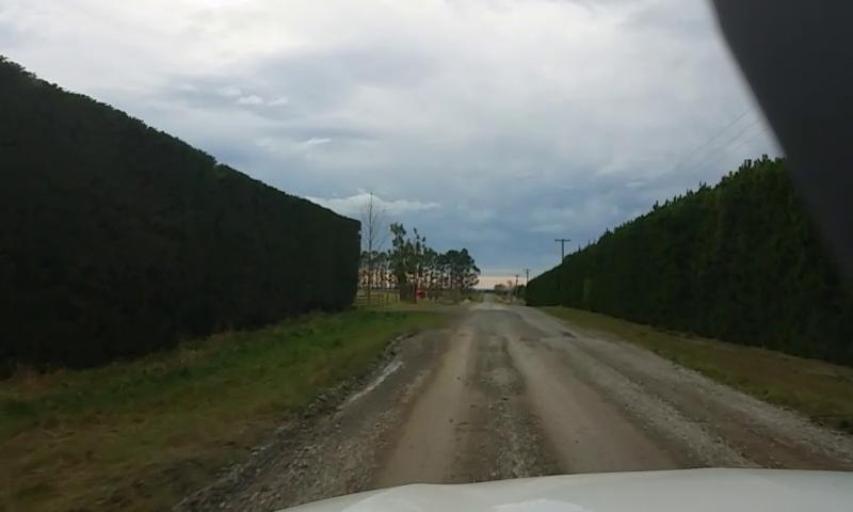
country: NZ
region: Canterbury
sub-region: Waimakariri District
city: Kaiapoi
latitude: -43.2911
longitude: 172.4588
